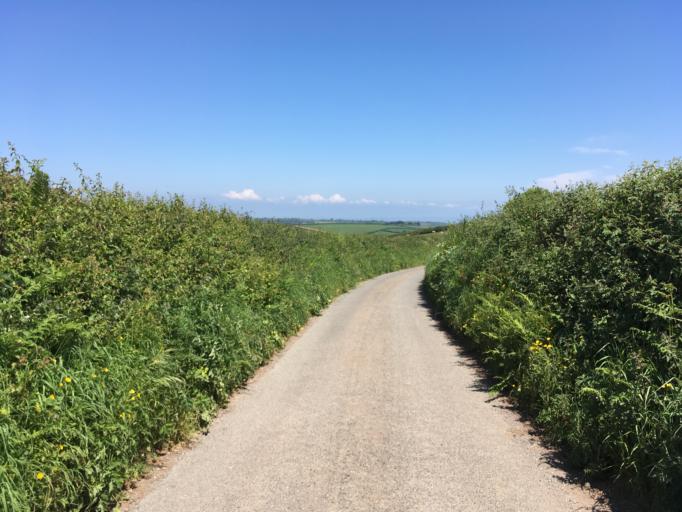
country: GB
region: England
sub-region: Devon
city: Dartmouth
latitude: 50.3493
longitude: -3.5407
